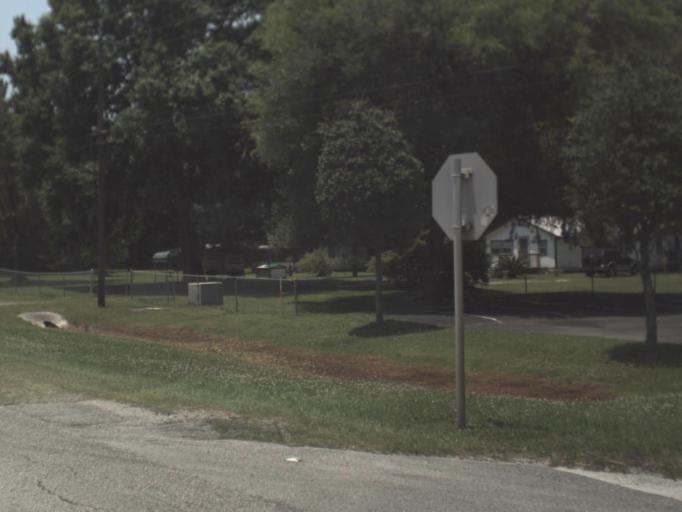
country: US
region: Florida
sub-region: Duval County
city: Baldwin
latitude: 30.1904
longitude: -82.0191
